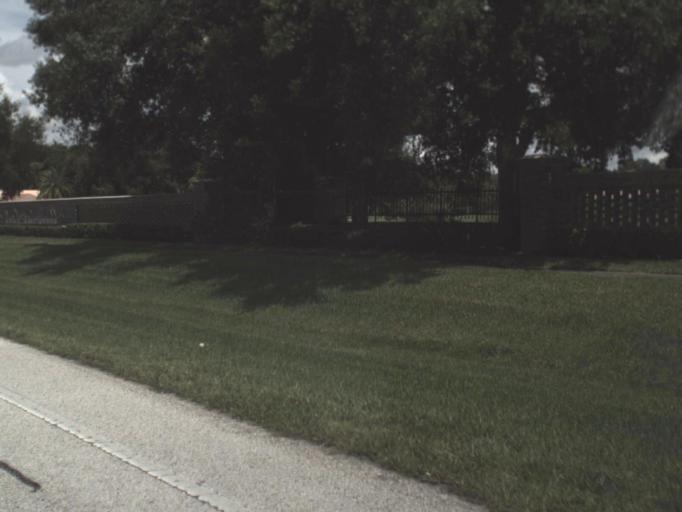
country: US
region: Florida
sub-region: Pasco County
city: Trinity
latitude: 28.1594
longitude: -82.6968
